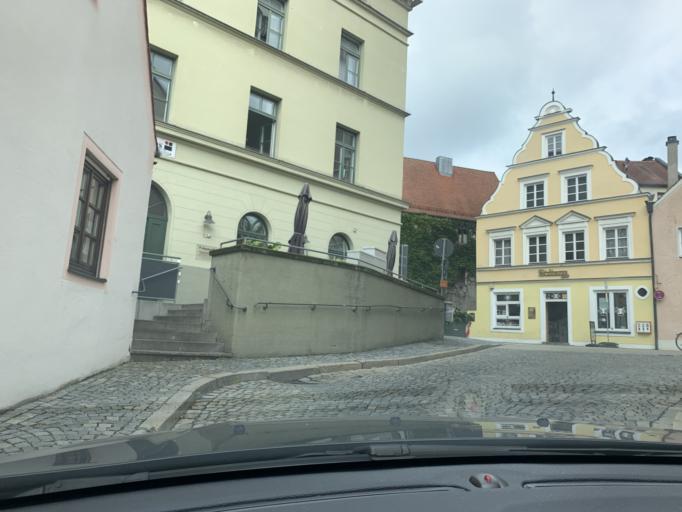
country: DE
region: Bavaria
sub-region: Upper Bavaria
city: Ingolstadt
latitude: 48.7638
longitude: 11.4194
